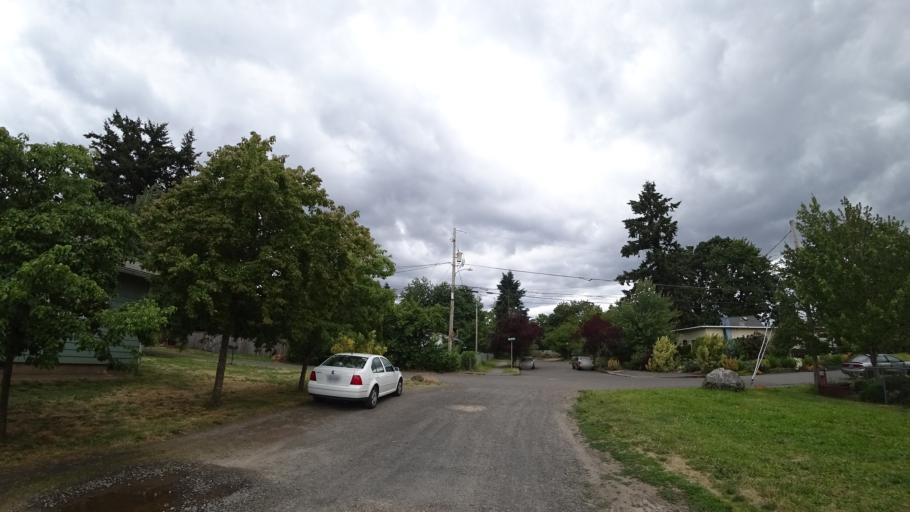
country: US
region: Oregon
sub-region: Multnomah County
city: Portland
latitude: 45.5604
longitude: -122.6139
